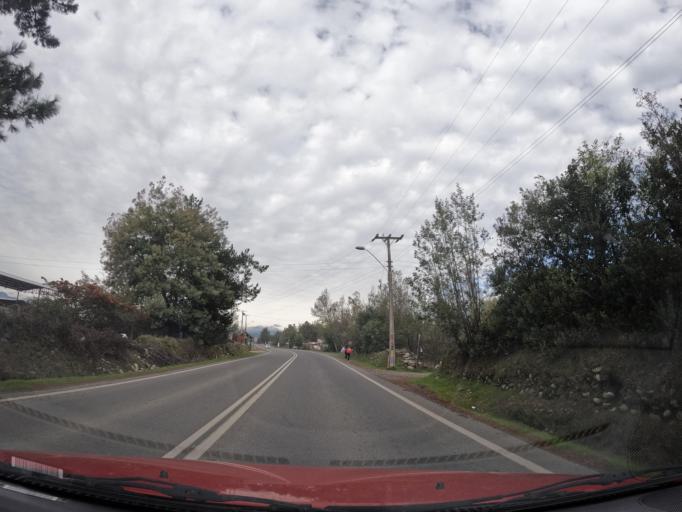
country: CL
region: Maule
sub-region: Provincia de Linares
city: Linares
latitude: -35.8987
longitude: -71.5172
